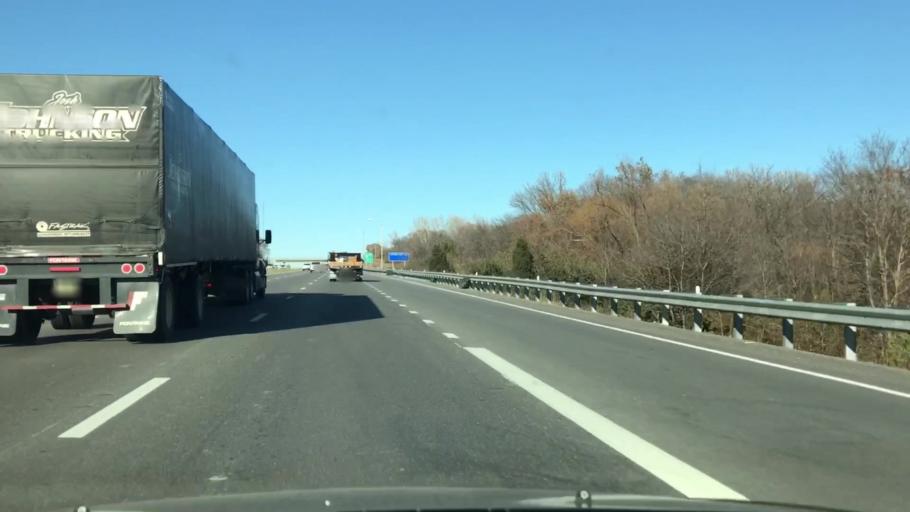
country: US
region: Missouri
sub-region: Jackson County
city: Raytown
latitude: 38.9977
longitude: -94.5021
